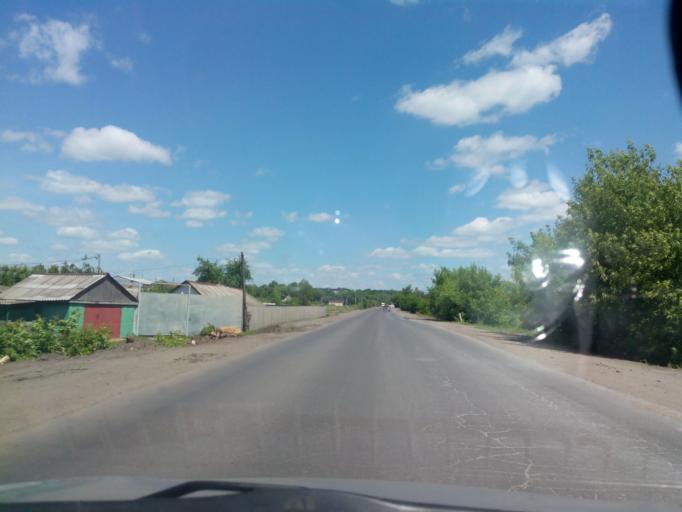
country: RU
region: Tambov
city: Zherdevka
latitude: 51.8126
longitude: 41.5055
